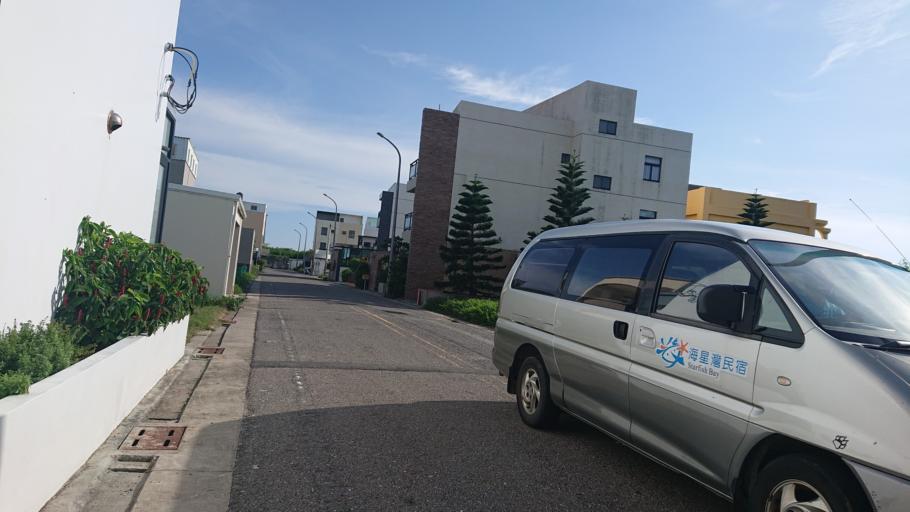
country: TW
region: Taiwan
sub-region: Penghu
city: Ma-kung
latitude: 23.5253
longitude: 119.5995
